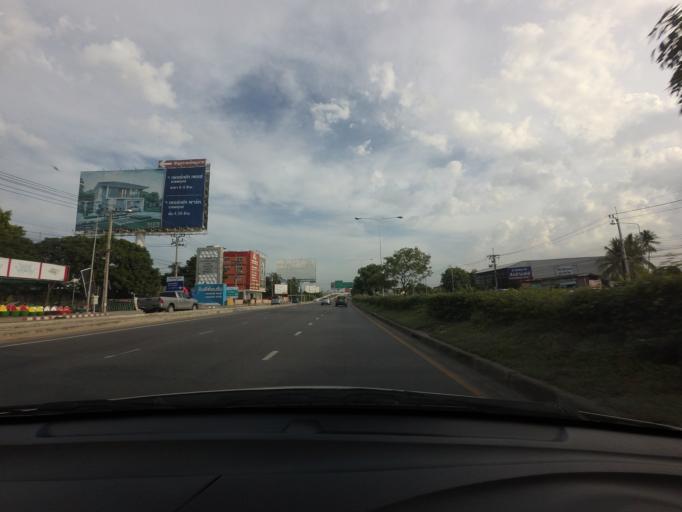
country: TH
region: Nonthaburi
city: Bang Bua Thong
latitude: 13.8608
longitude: 100.4514
